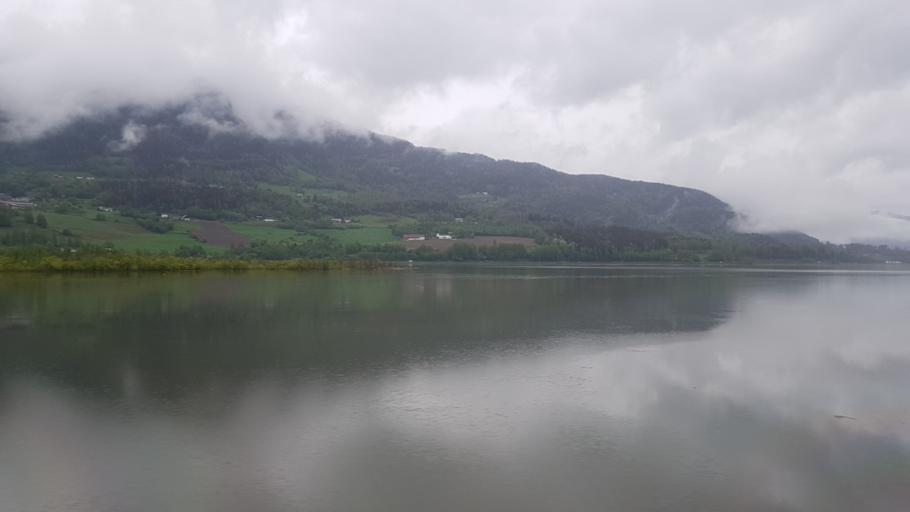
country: NO
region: Oppland
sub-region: Oyer
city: Tretten
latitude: 61.4262
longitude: 10.2261
